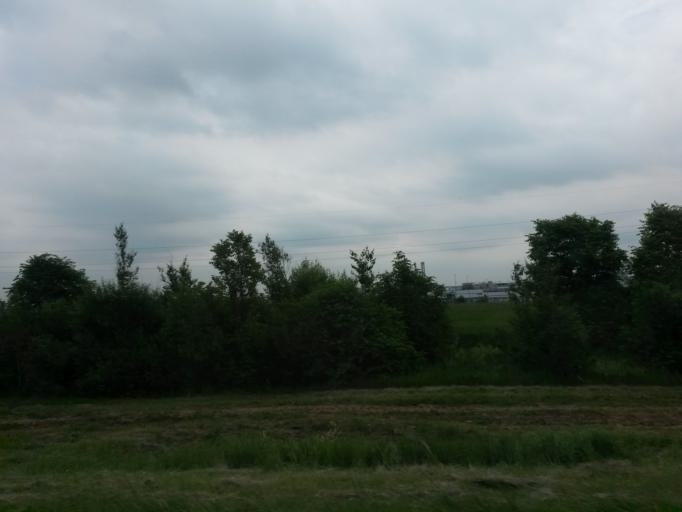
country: RU
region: Moskovskaya
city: Lyubuchany
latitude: 55.2553
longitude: 37.5318
